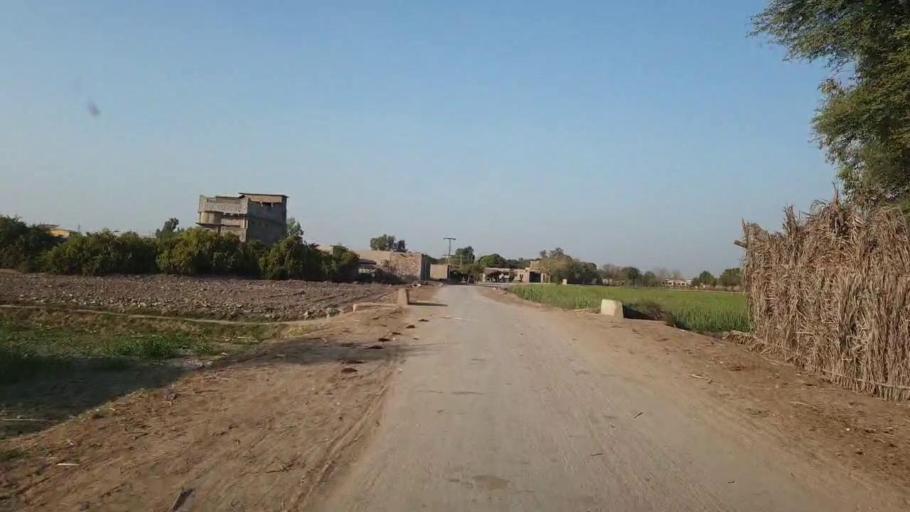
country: PK
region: Sindh
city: Tando Allahyar
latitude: 25.3522
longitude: 68.7053
